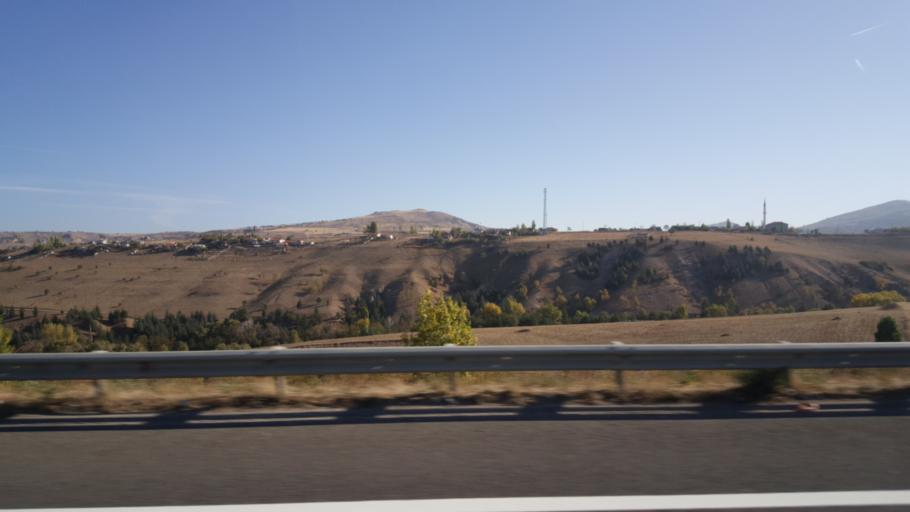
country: TR
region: Ankara
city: Mamak
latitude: 39.9866
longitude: 32.9513
